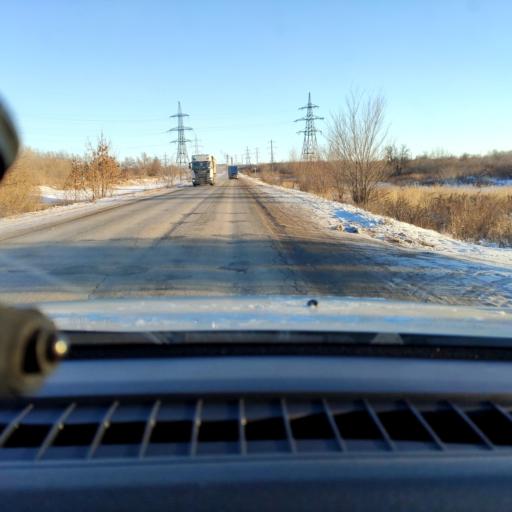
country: RU
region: Samara
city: Chapayevsk
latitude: 53.0037
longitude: 49.7498
